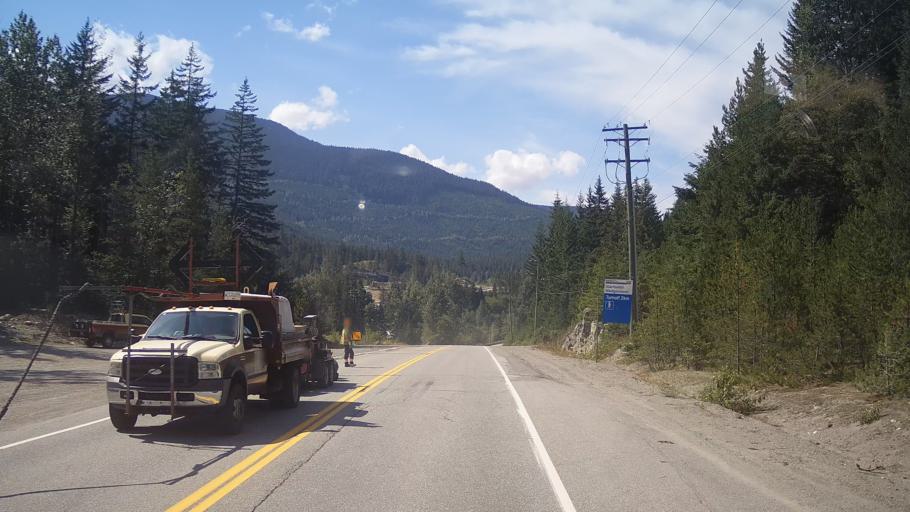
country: CA
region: British Columbia
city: Whistler
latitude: 50.1824
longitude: -122.8749
